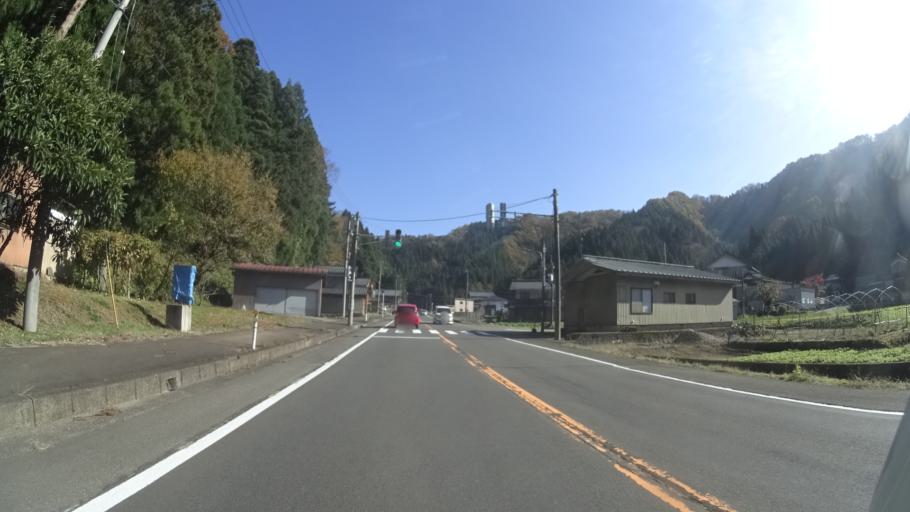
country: JP
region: Fukui
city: Ono
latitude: 35.9933
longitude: 136.4469
